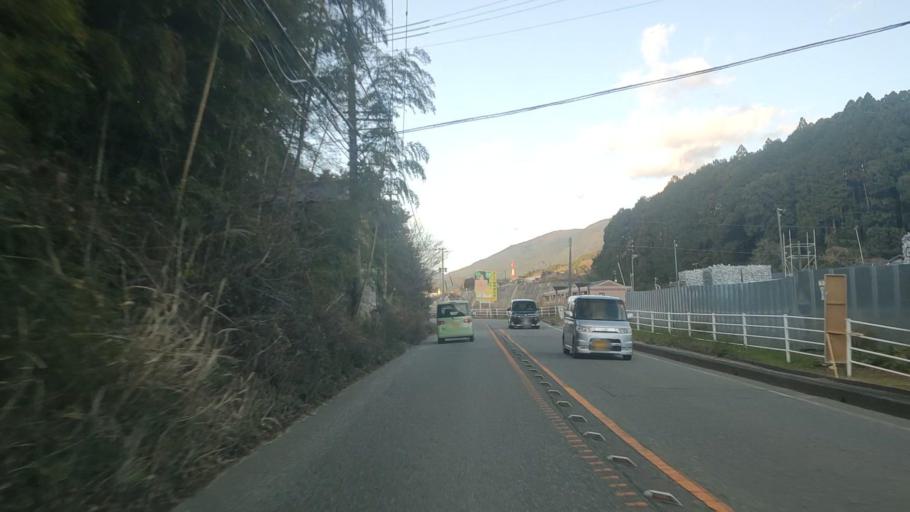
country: JP
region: Fukuoka
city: Dazaifu
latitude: 33.5410
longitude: 130.5394
